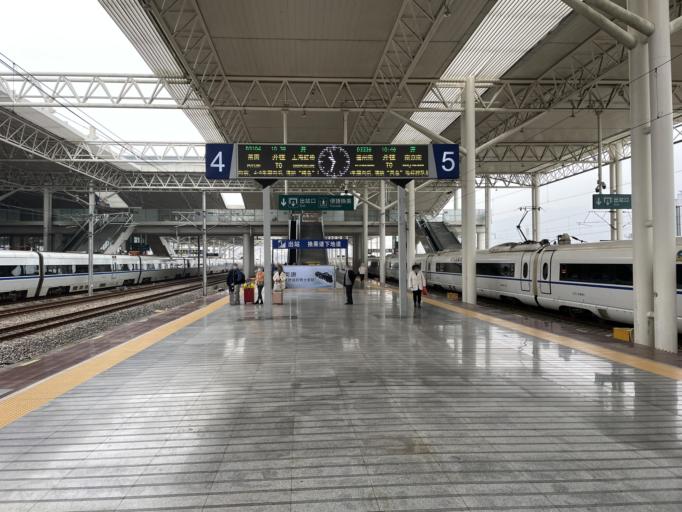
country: CN
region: Zhejiang Sheng
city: Shiqiao
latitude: 27.9702
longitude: 120.5810
